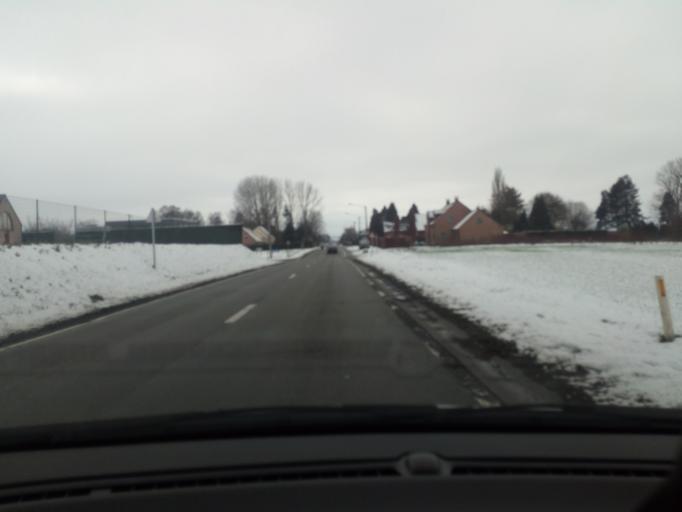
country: BE
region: Wallonia
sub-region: Province du Hainaut
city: Estinnes-au-Val
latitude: 50.3893
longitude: 4.0763
